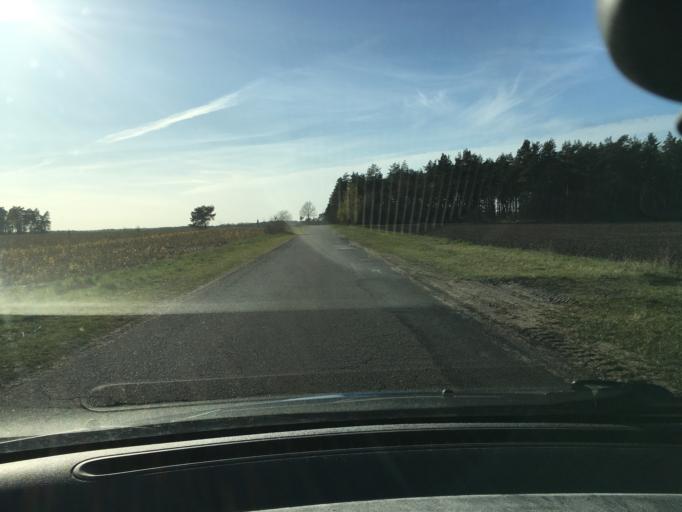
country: DE
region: Lower Saxony
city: Bispingen
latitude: 53.1111
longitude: 10.0159
